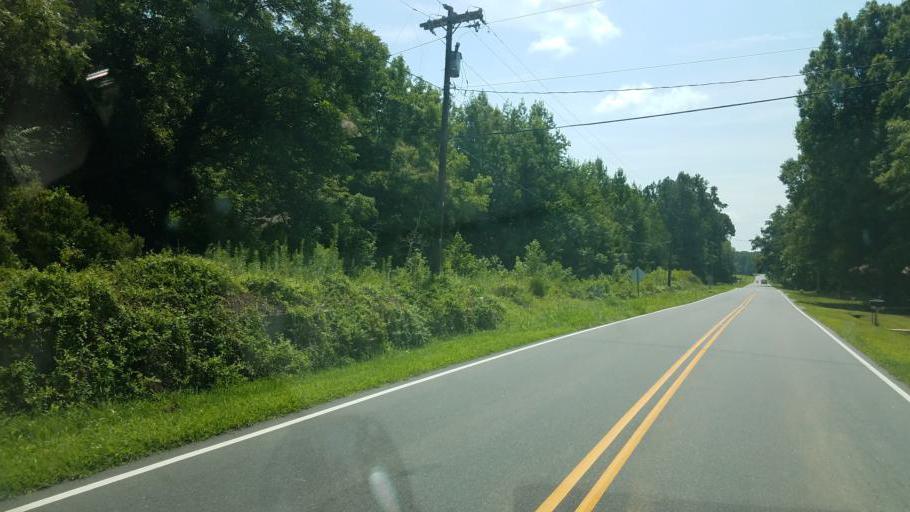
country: US
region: North Carolina
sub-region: Gaston County
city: Cherryville
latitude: 35.3648
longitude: -81.3661
